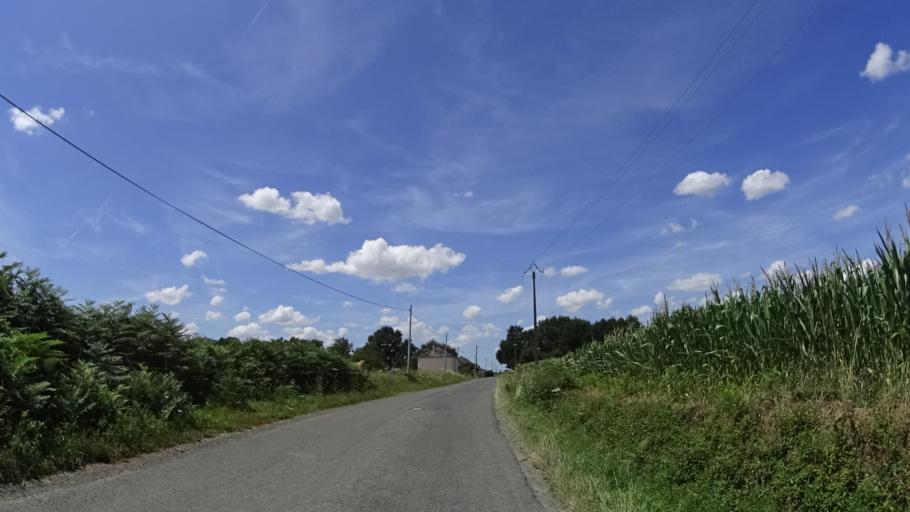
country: FR
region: Pays de la Loire
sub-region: Departement de Maine-et-Loire
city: Segre
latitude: 47.6376
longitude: -0.8640
